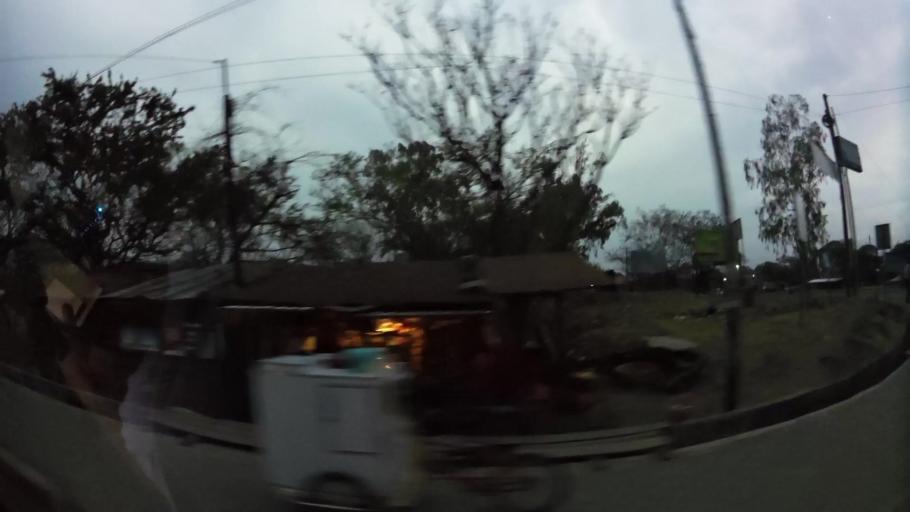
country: NI
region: Esteli
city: Esteli
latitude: 13.1075
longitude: -86.3582
